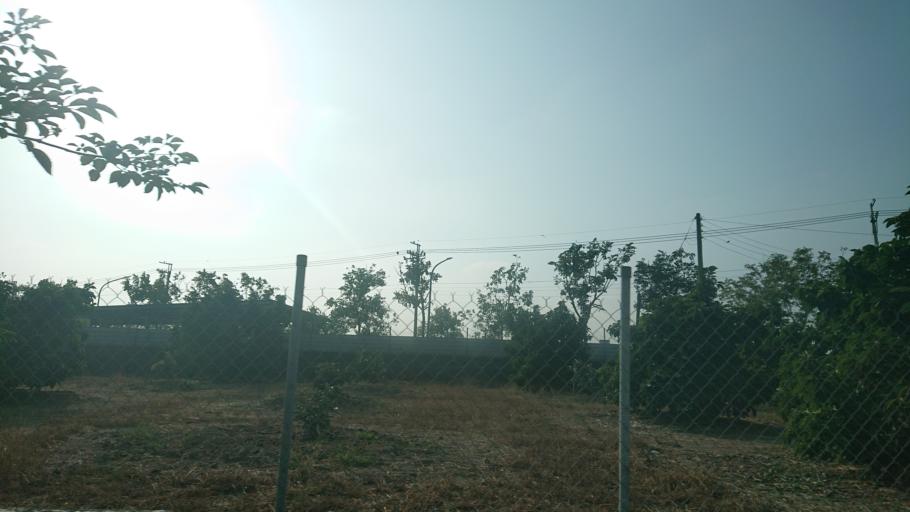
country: TW
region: Taiwan
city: Xinying
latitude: 23.2036
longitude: 120.2710
